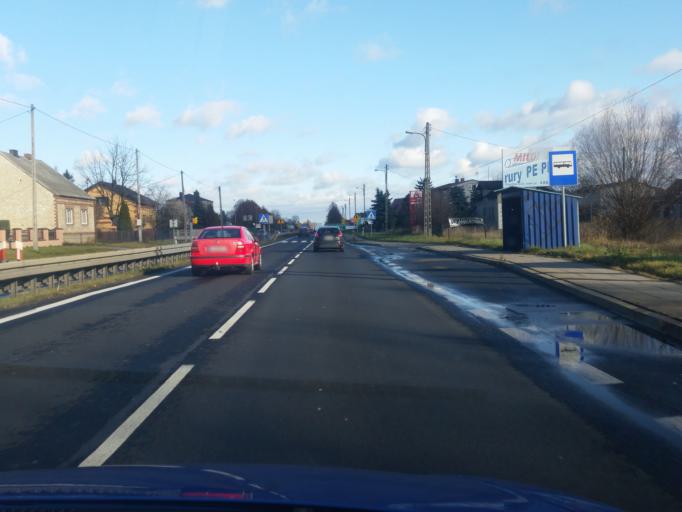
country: PL
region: Silesian Voivodeship
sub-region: Powiat czestochowski
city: Kamienica Polska
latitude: 50.6898
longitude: 19.1345
